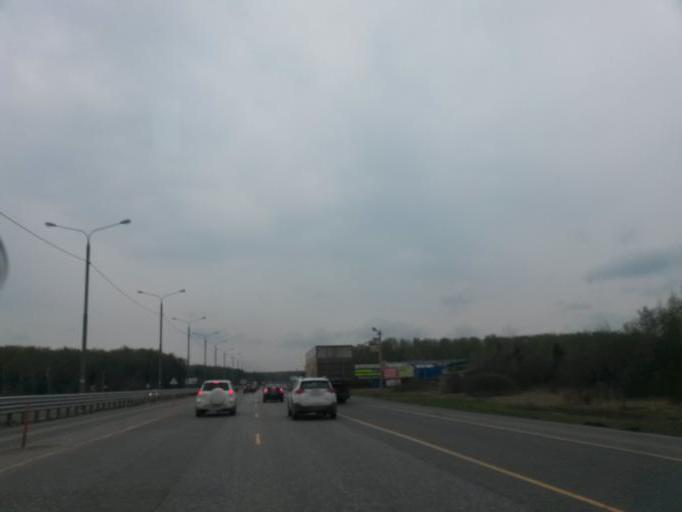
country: RU
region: Moskovskaya
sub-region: Podol'skiy Rayon
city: Podol'sk
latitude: 55.3752
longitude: 37.6043
